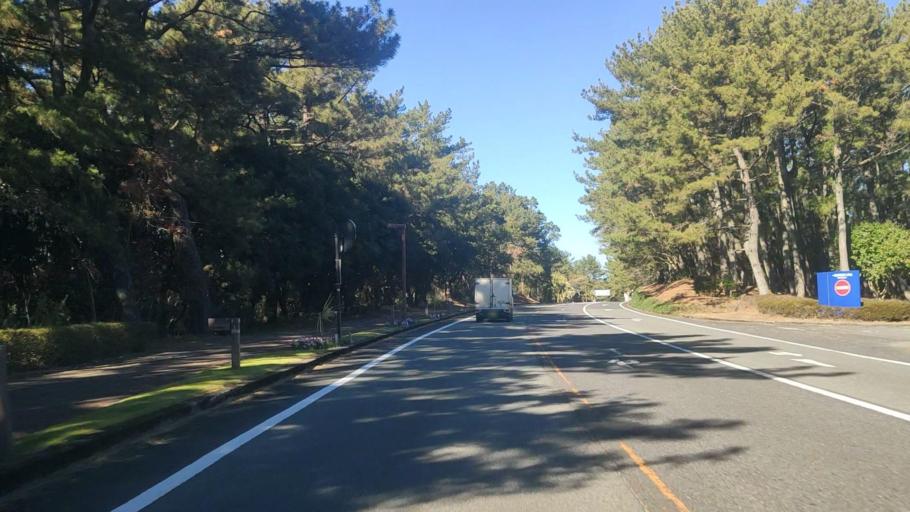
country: JP
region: Miyazaki
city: Miyazaki-shi
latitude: 31.9557
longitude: 131.4672
